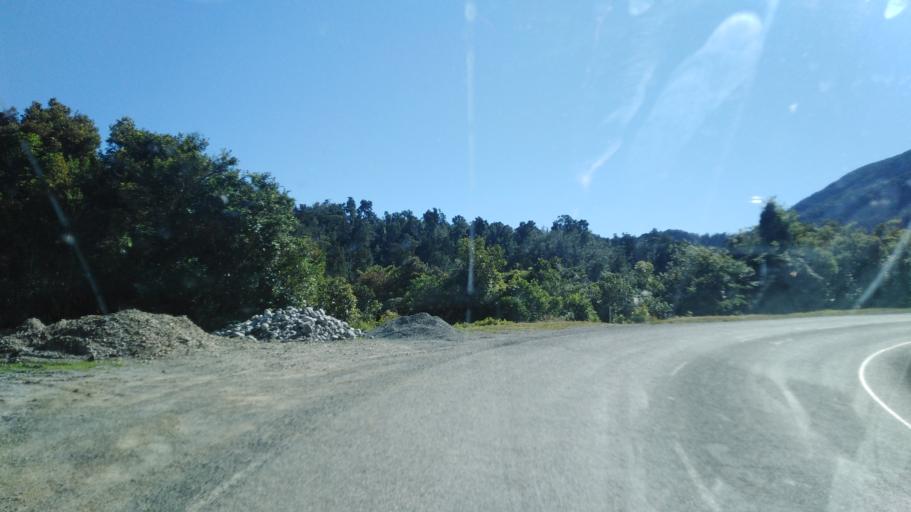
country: NZ
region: West Coast
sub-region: Buller District
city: Westport
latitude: -41.5264
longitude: 172.0014
